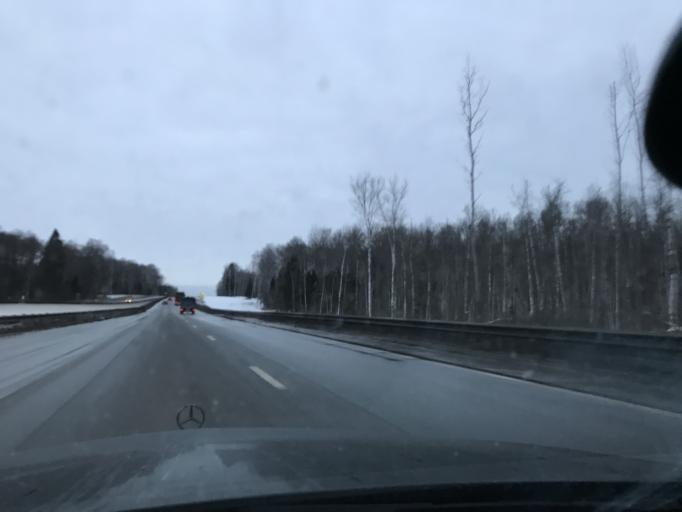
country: RU
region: Vladimir
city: Kosterevo
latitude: 55.9542
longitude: 39.5922
